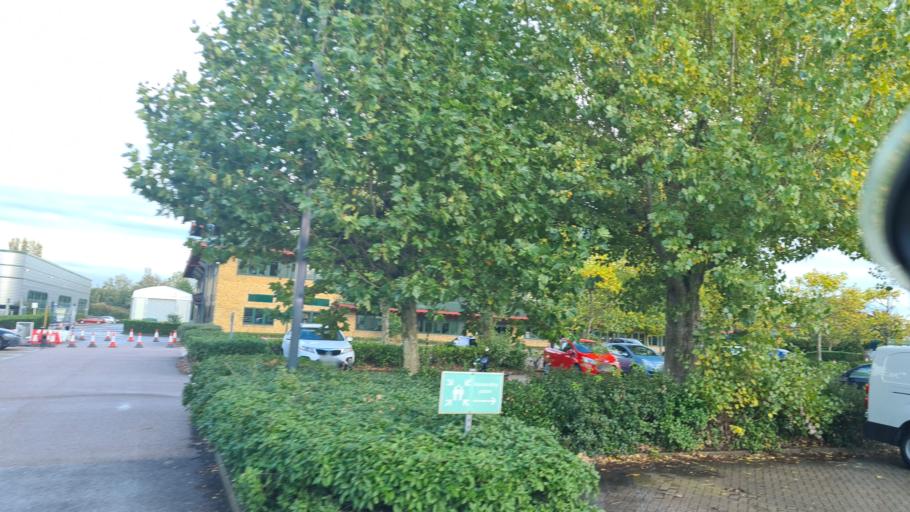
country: GB
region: England
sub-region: West Sussex
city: Littlehampton
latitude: 50.8218
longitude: -0.5290
